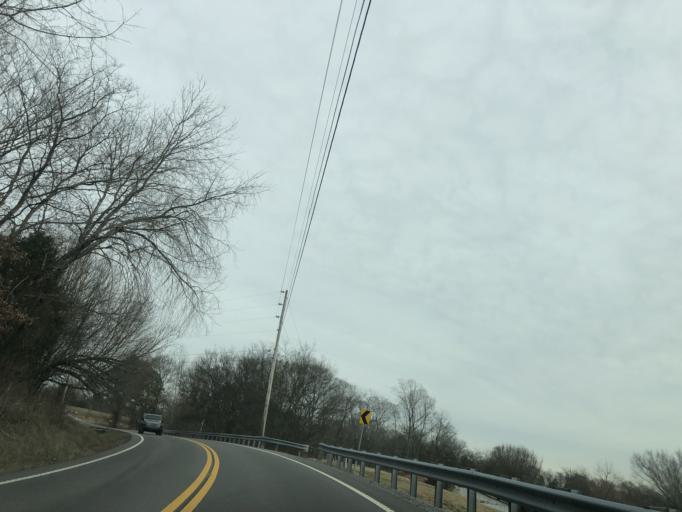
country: US
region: Tennessee
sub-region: Robertson County
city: Greenbrier
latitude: 36.4808
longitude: -86.7867
